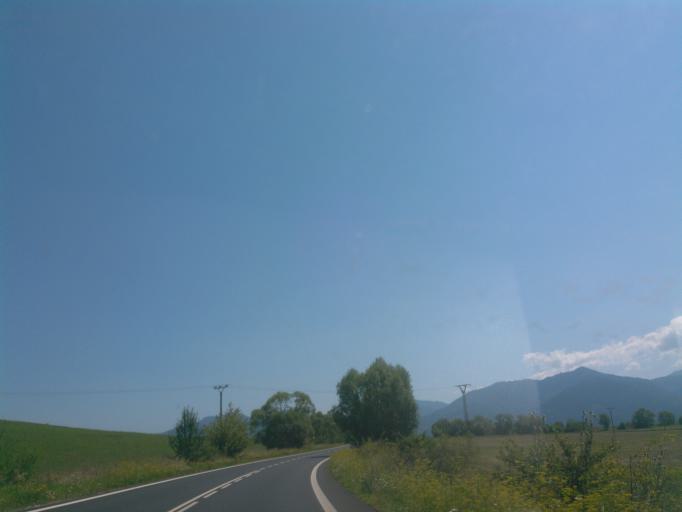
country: SK
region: Zilinsky
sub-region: Okres Liptovsky Mikulas
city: Liptovsky Mikulas
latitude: 49.0605
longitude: 19.4826
